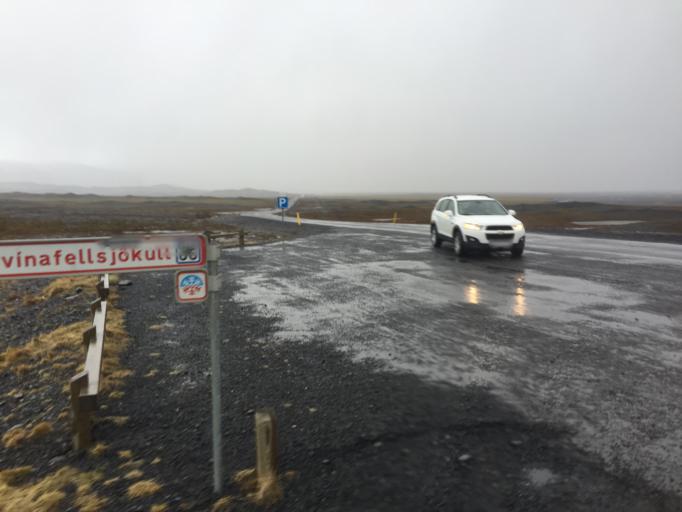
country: IS
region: East
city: Hoefn
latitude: 64.0060
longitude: -16.9281
